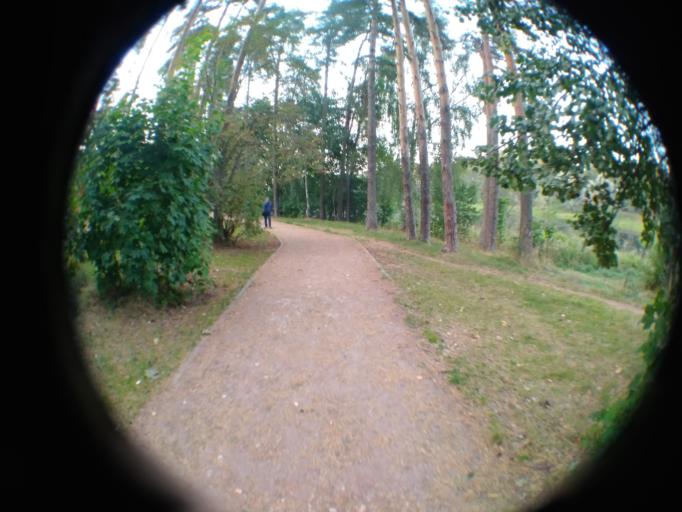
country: RU
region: Moskovskaya
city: Kratovo
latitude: 55.5878
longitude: 38.1582
